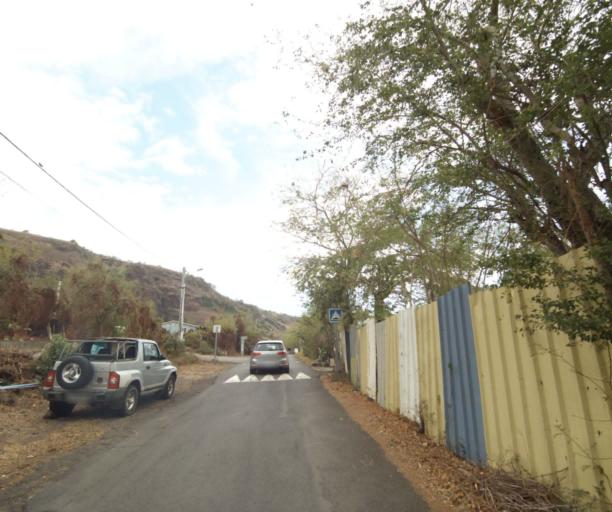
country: RE
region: Reunion
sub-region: Reunion
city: Saint-Paul
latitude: -21.0024
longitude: 55.3003
